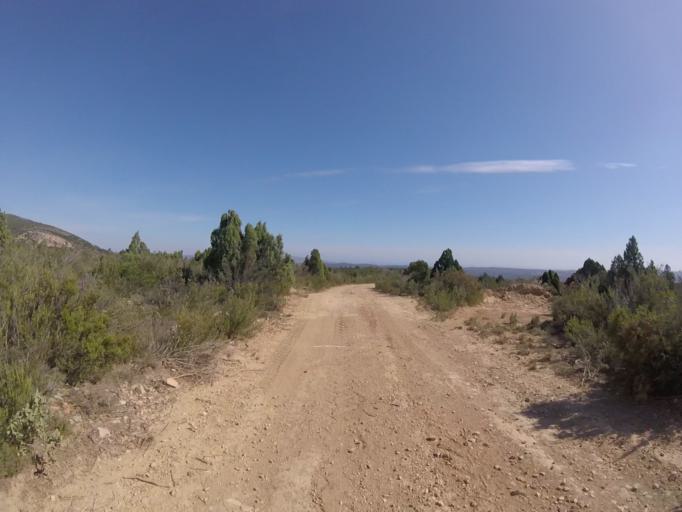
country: ES
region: Valencia
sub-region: Provincia de Castello
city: Sierra-Engarceran
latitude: 40.2717
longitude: 0.0218
